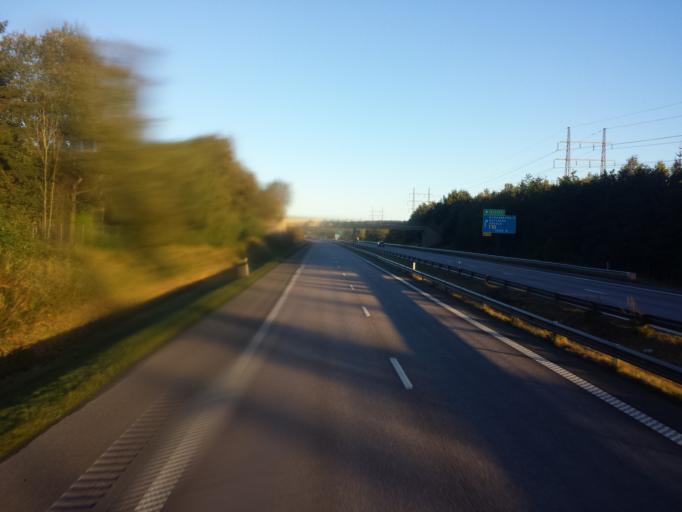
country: SE
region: Halland
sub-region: Kungsbacka Kommun
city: Kungsbacka
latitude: 57.4628
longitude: 12.0767
